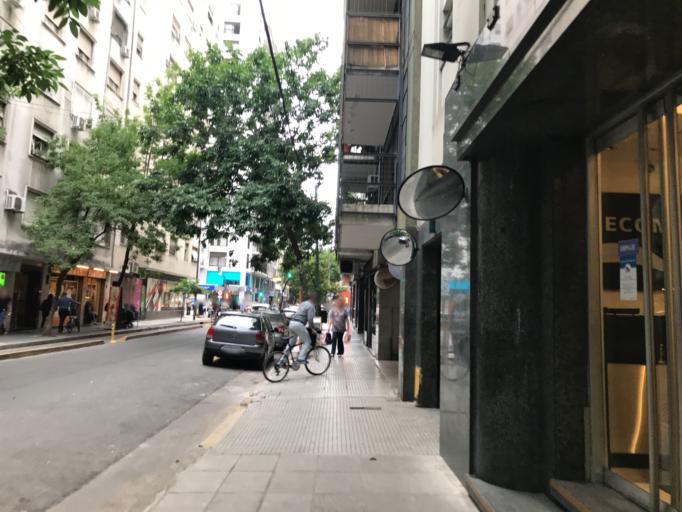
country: AR
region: Buenos Aires F.D.
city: Retiro
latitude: -34.5935
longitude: -58.4033
